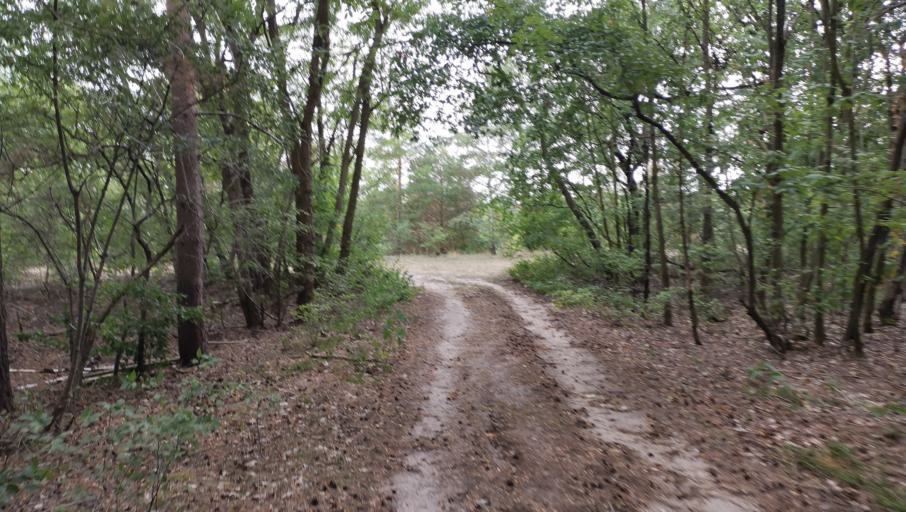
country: DE
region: Brandenburg
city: Potsdam
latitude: 52.3684
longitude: 13.0367
